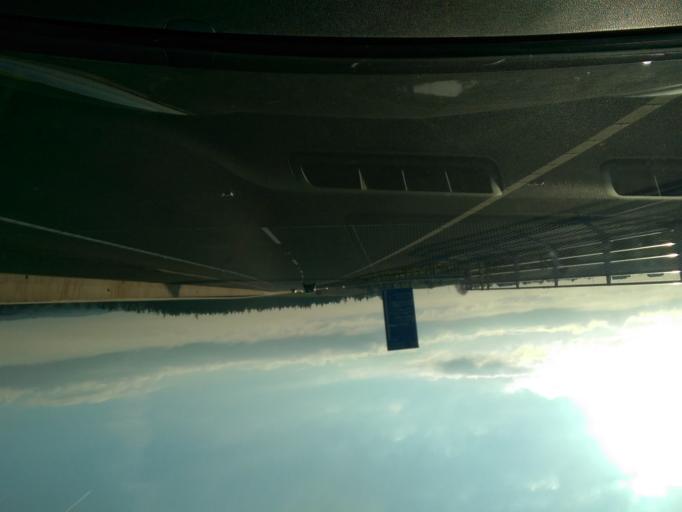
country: IE
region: Munster
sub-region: North Tipperary
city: Templemore
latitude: 52.8866
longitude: -7.9248
